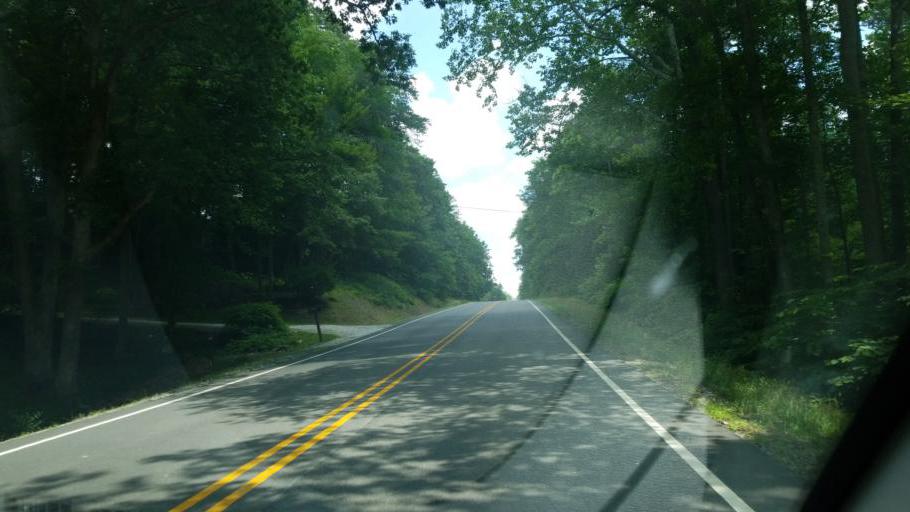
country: US
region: Virginia
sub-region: Cumberland County
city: Cumberland
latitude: 37.4828
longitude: -78.3157
